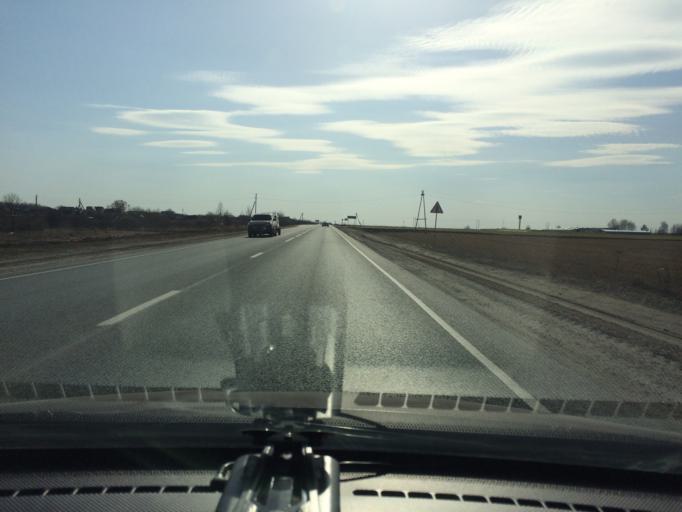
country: RU
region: Mariy-El
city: Yoshkar-Ola
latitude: 56.6717
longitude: 48.0045
